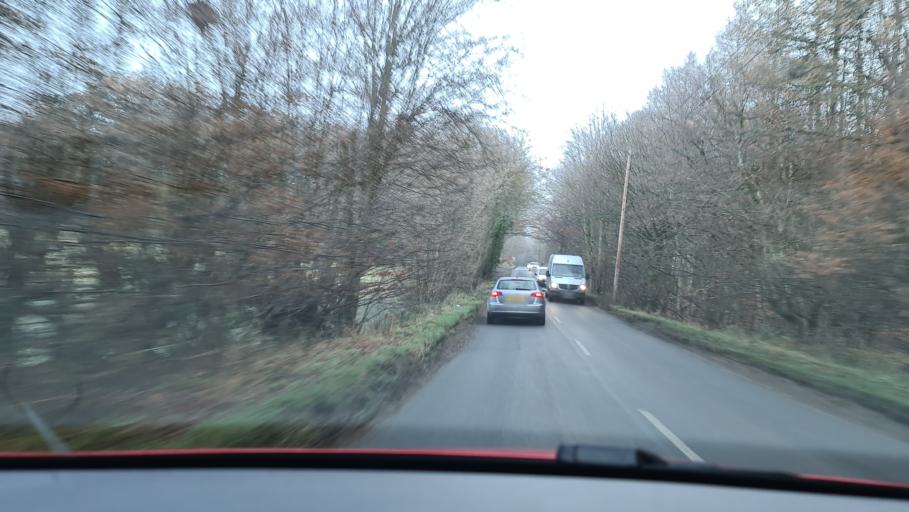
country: GB
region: England
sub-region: Buckinghamshire
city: Seer Green
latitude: 51.6042
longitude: -0.6009
